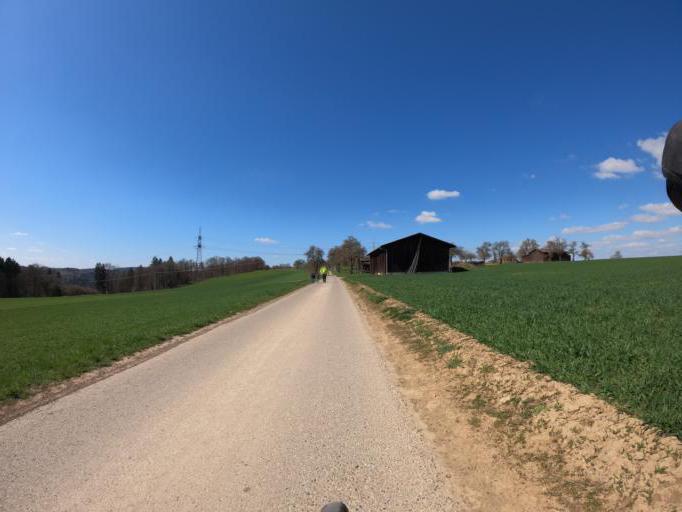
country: DE
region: Baden-Wuerttemberg
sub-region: Tuebingen Region
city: Rottenburg
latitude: 48.4680
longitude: 8.8887
